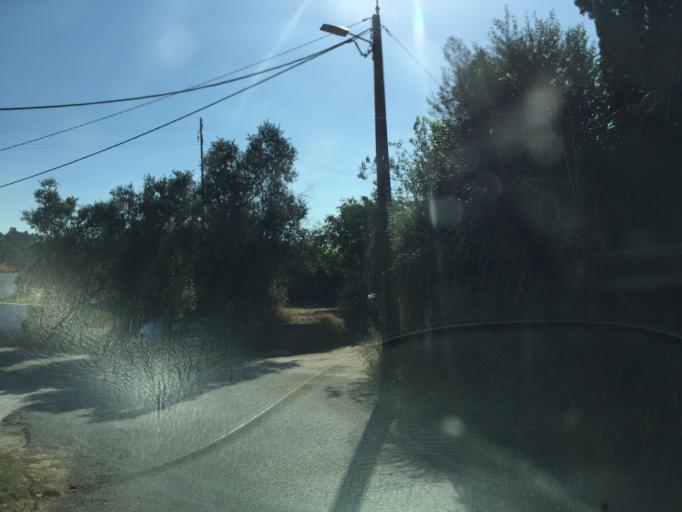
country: PT
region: Santarem
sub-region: Ferreira do Zezere
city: Ferreira do Zezere
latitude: 39.5988
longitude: -8.2989
